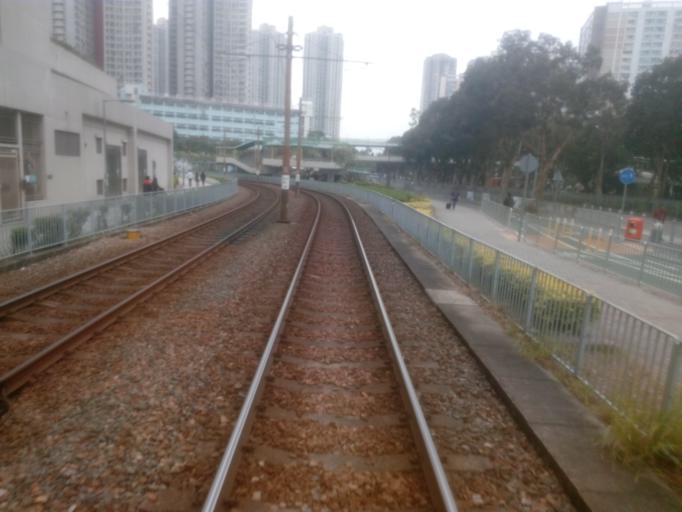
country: HK
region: Tuen Mun
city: Tuen Mun
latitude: 22.3754
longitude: 113.9668
